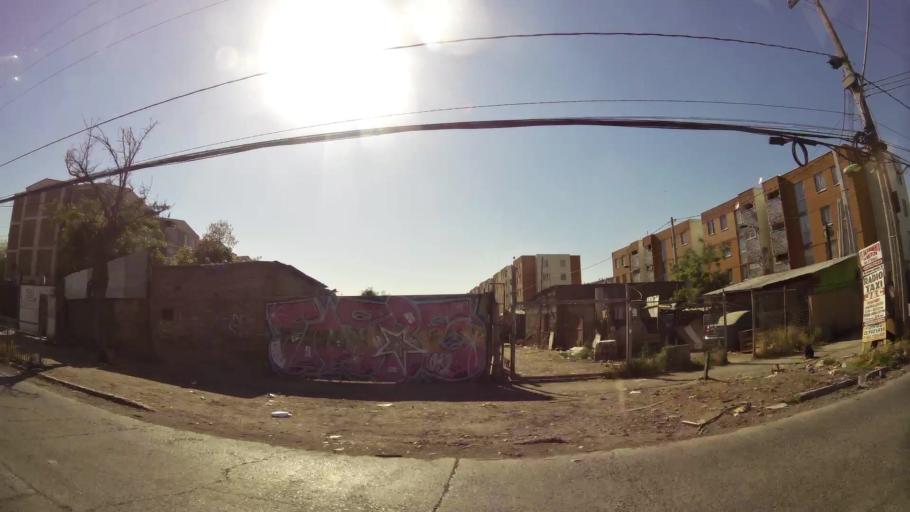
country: CL
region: Santiago Metropolitan
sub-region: Provincia de Maipo
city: San Bernardo
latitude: -33.5544
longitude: -70.6923
